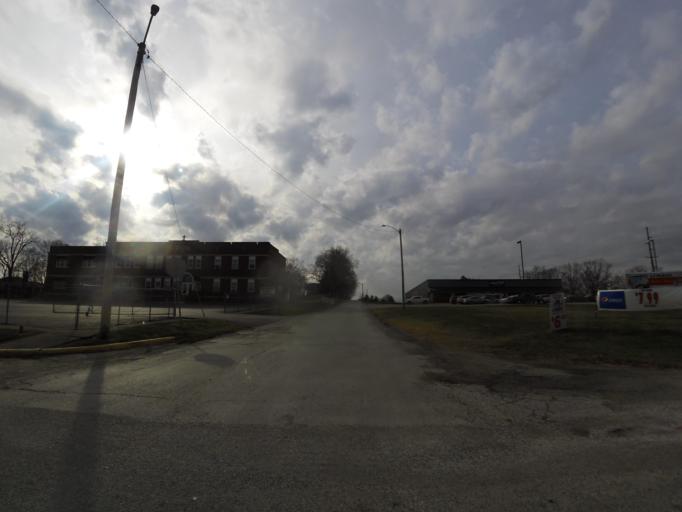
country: US
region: Illinois
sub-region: Christian County
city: Pana
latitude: 39.3868
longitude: -89.0837
